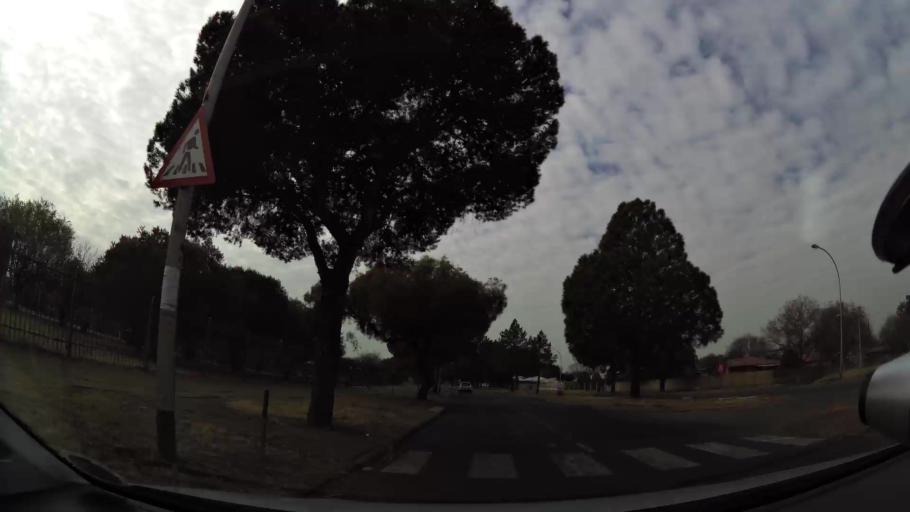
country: ZA
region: Orange Free State
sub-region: Mangaung Metropolitan Municipality
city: Bloemfontein
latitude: -29.1306
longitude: 26.1946
